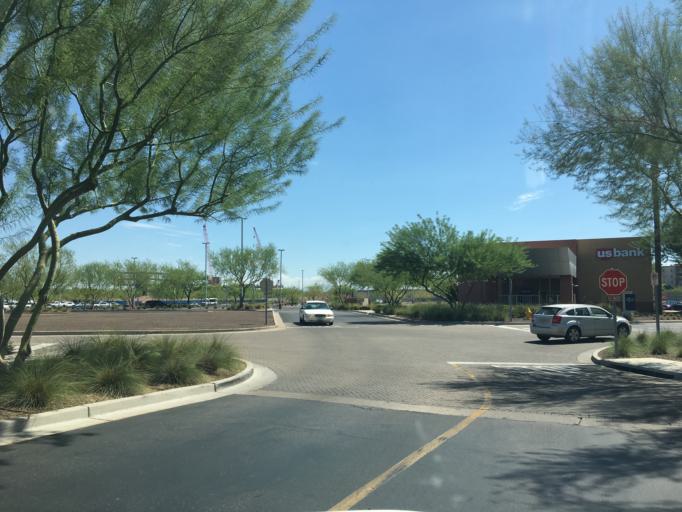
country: US
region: Arizona
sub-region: Maricopa County
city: Tempe
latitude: 33.4317
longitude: -111.9025
